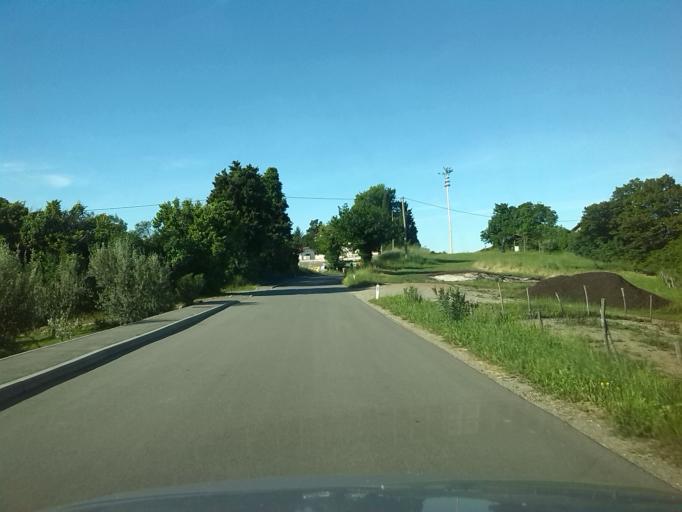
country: SI
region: Brda
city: Dobrovo
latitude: 45.9829
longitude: 13.5205
